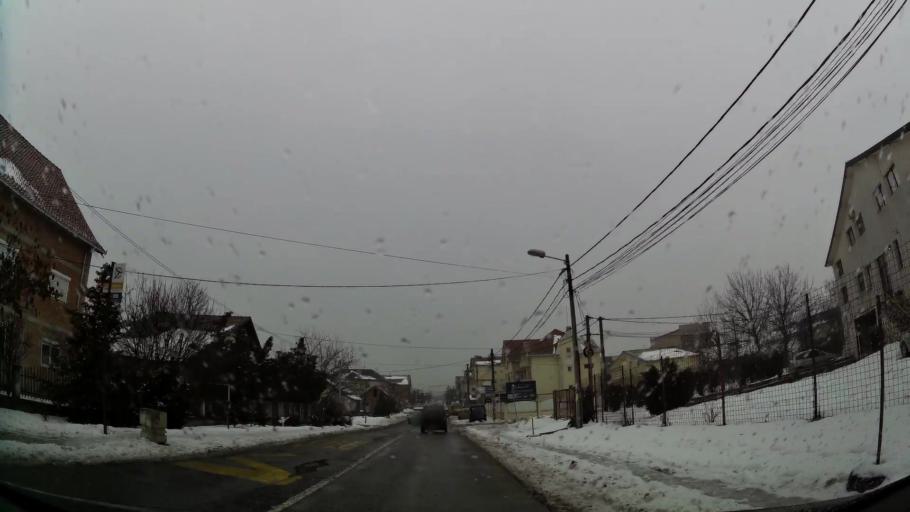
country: RS
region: Central Serbia
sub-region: Belgrade
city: Zemun
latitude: 44.8523
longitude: 20.3485
